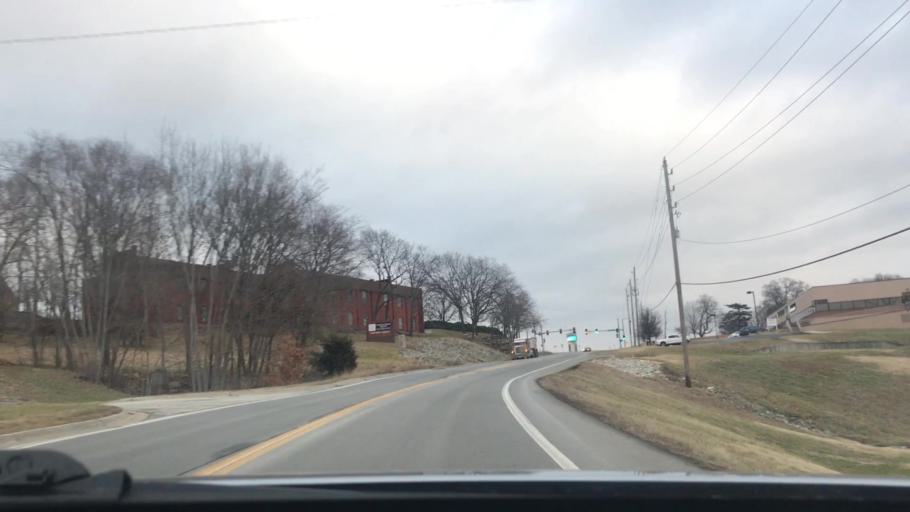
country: US
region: Missouri
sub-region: Platte County
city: Platte City
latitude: 39.3671
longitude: -94.7773
